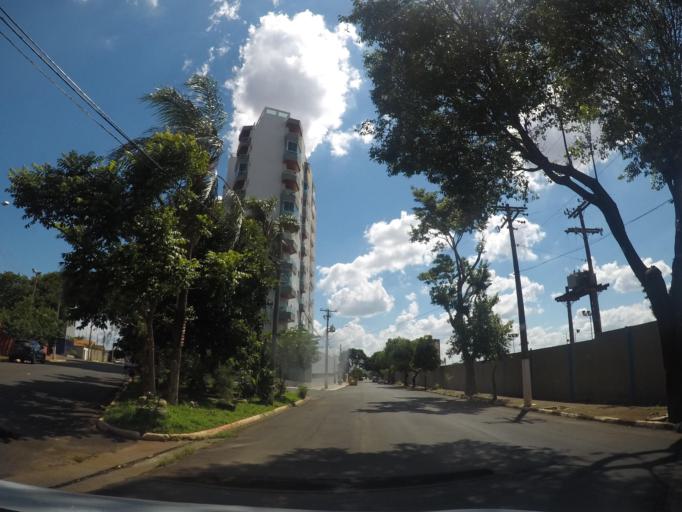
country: BR
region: Sao Paulo
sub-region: Sumare
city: Sumare
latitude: -22.8303
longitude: -47.2721
